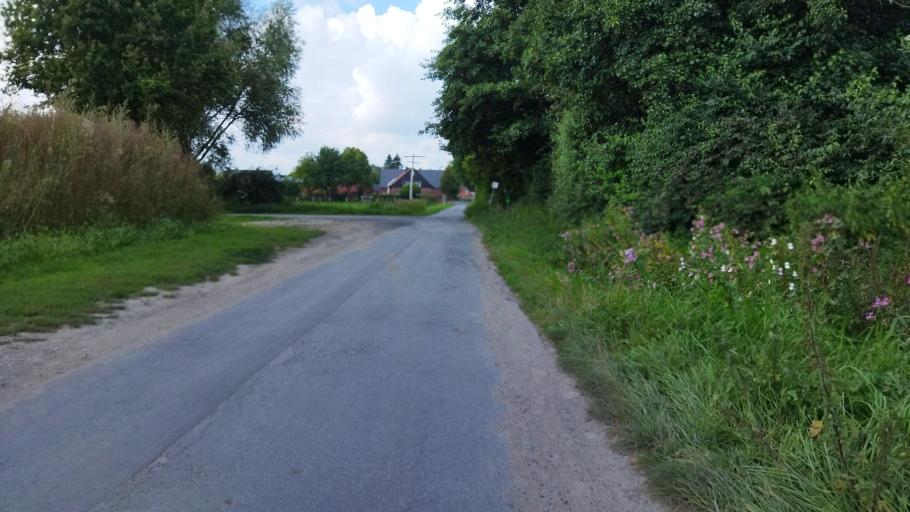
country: DE
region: North Rhine-Westphalia
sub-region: Regierungsbezirk Munster
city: Telgte
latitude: 51.9801
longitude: 7.8011
